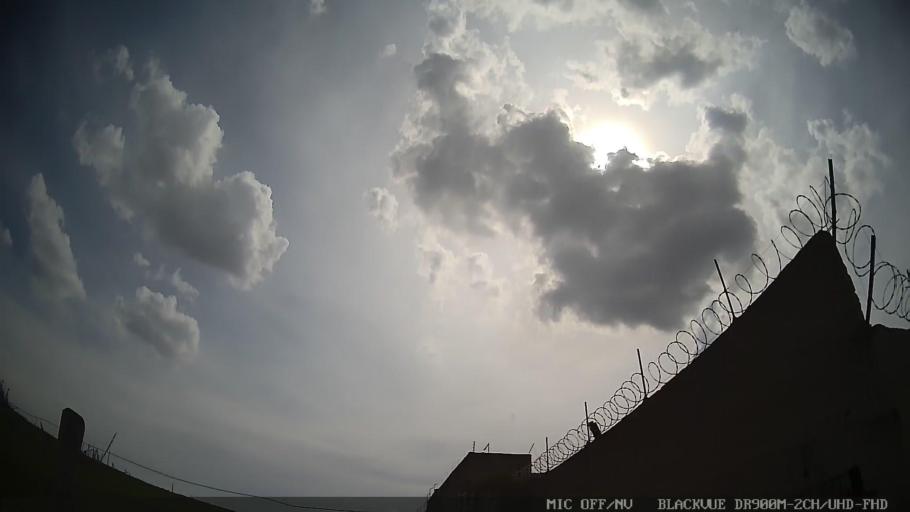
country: BR
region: Sao Paulo
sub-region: Braganca Paulista
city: Braganca Paulista
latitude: -22.9397
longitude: -46.5141
